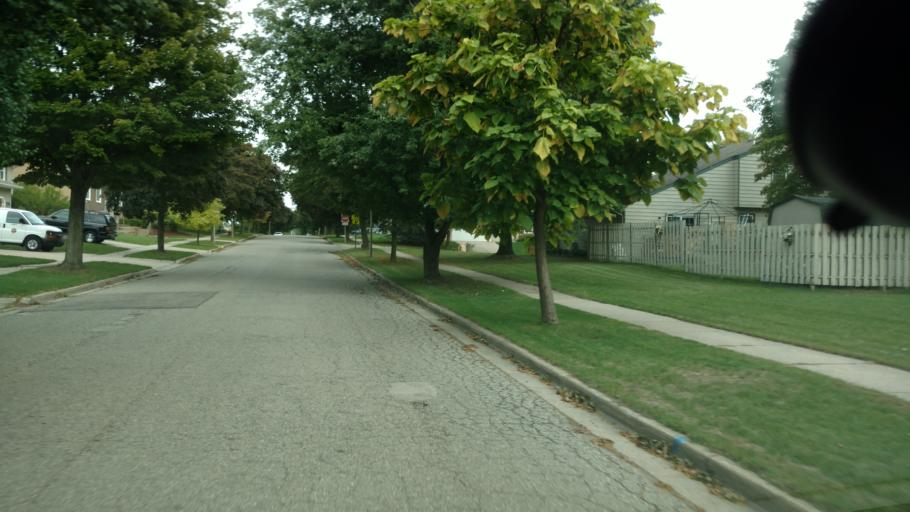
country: US
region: Michigan
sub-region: Ingham County
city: East Lansing
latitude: 42.7586
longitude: -84.5197
